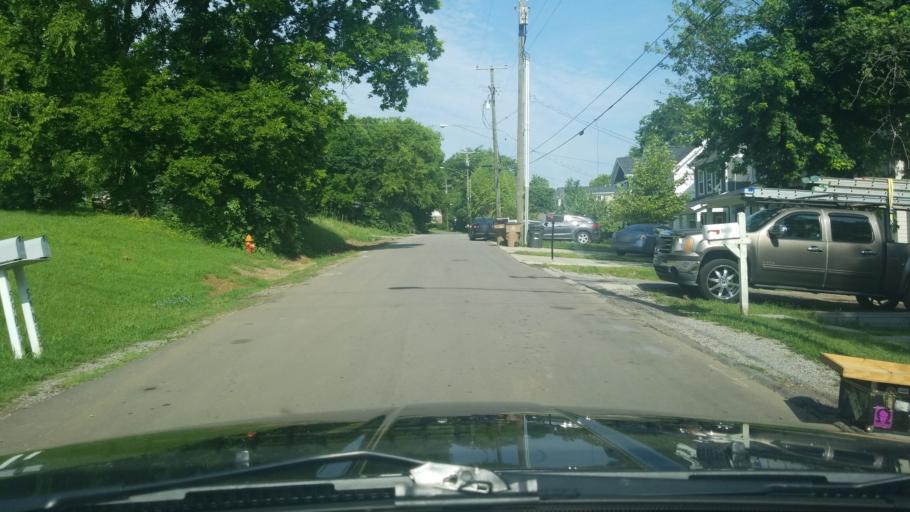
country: US
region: Tennessee
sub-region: Davidson County
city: Belle Meade
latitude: 36.1539
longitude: -86.8645
